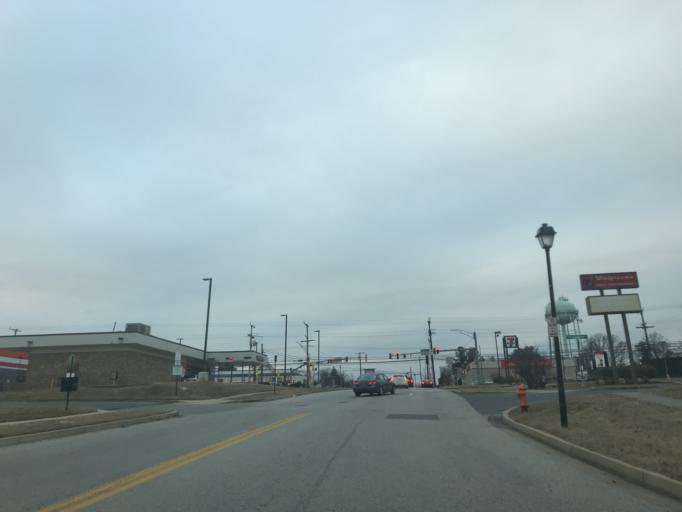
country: US
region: Maryland
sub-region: Baltimore County
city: Randallstown
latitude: 39.3701
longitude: -76.7986
